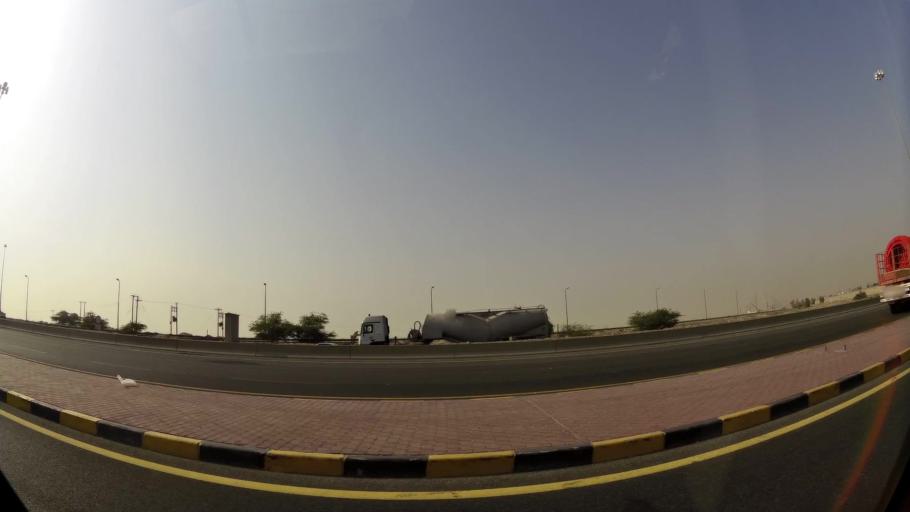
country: KW
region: Al Asimah
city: Ar Rabiyah
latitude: 29.2534
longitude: 47.8634
